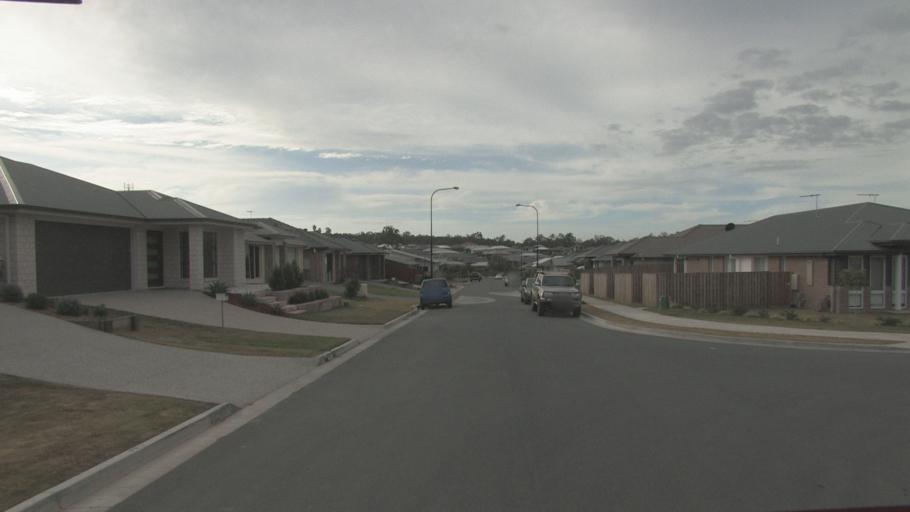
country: AU
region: Queensland
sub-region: Logan
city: Windaroo
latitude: -27.7210
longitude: 153.1648
